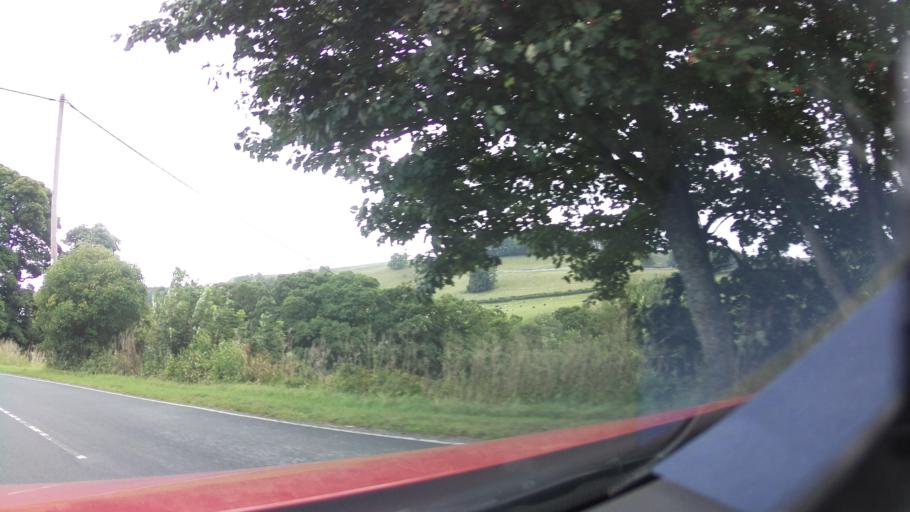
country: GB
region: England
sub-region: North Yorkshire
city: Leyburn
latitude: 54.3955
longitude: -1.8274
